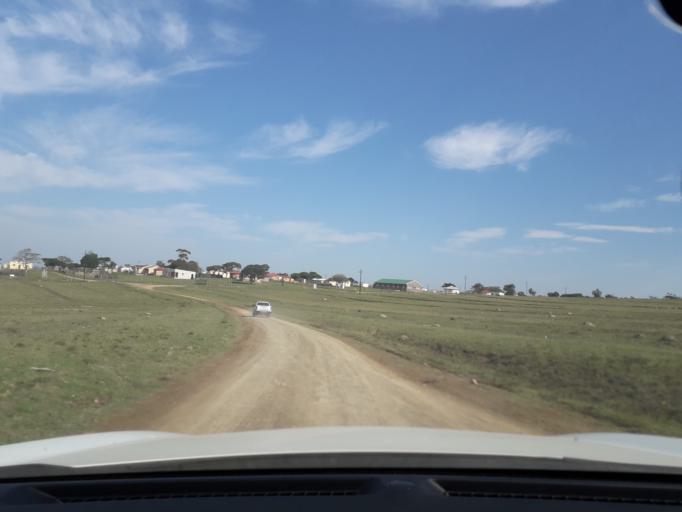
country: ZA
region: Eastern Cape
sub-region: Buffalo City Metropolitan Municipality
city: Bhisho
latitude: -33.0061
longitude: 27.3099
